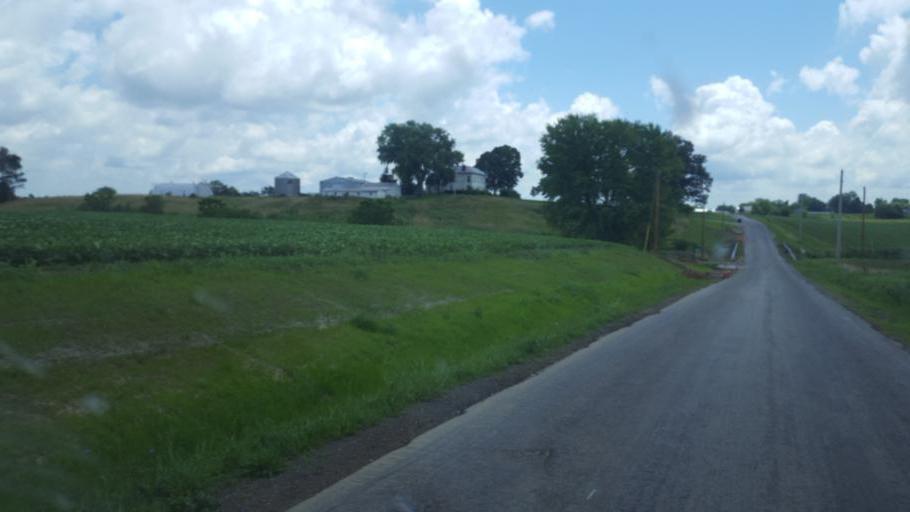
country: US
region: Ohio
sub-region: Highland County
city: Greenfield
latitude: 39.2677
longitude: -83.4538
